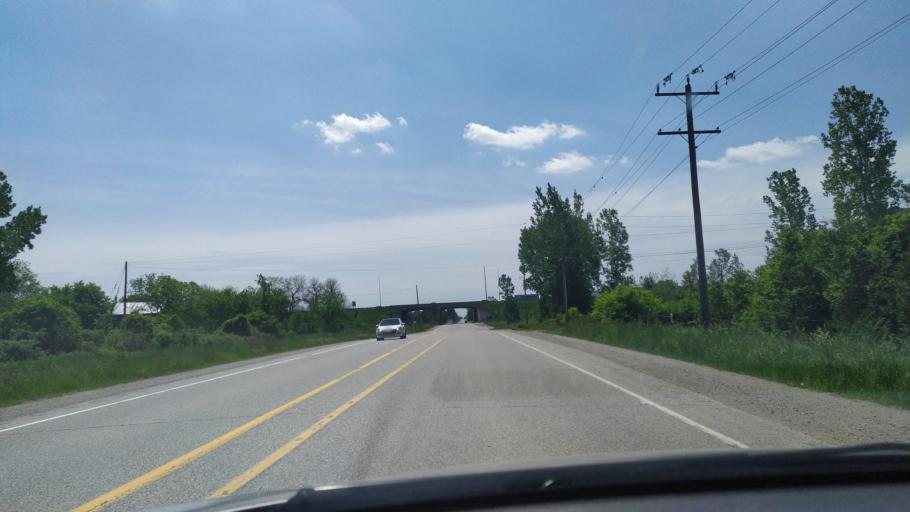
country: CA
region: Ontario
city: Ingersoll
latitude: 42.9788
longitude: -80.9513
